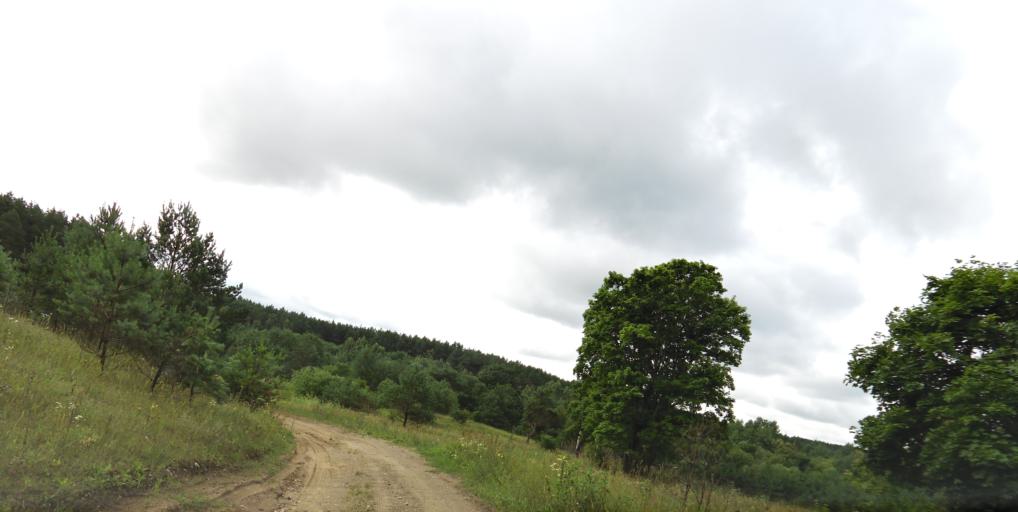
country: LT
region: Vilnius County
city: Pilaite
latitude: 54.7001
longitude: 25.1942
